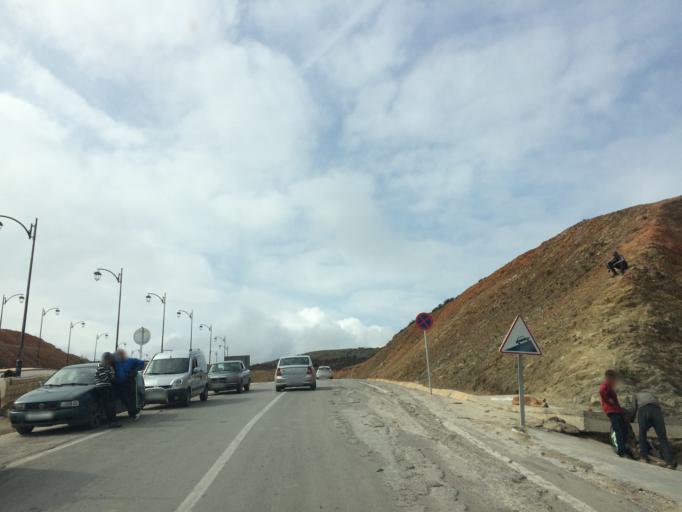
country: ES
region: Ceuta
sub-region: Ceuta
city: Ceuta
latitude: 35.8668
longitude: -5.3455
